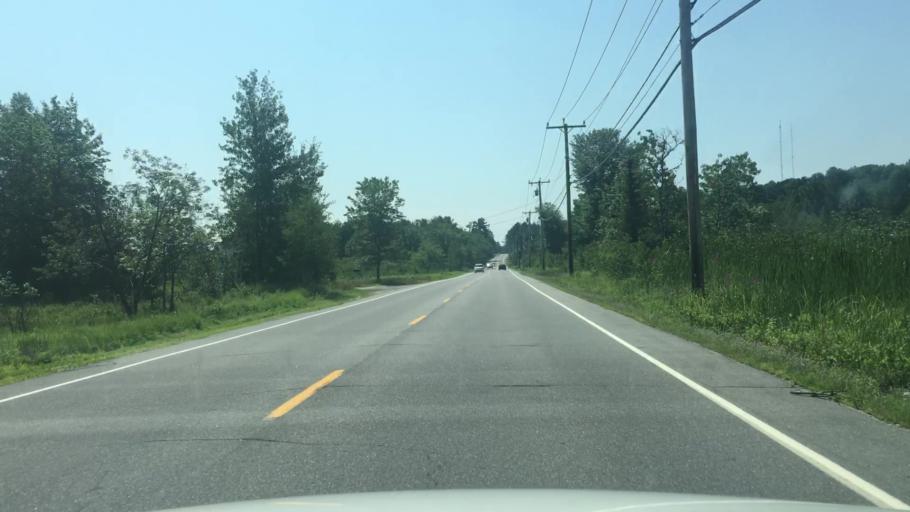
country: US
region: Maine
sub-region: Cumberland County
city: Cumberland Center
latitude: 43.8700
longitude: -70.3257
